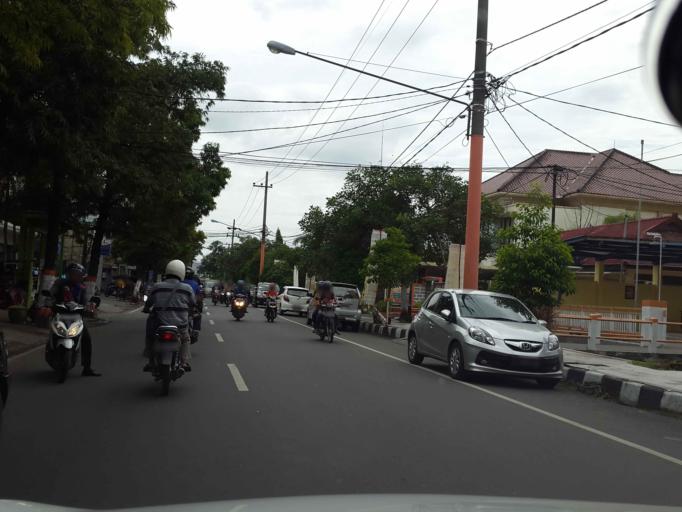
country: ID
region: East Java
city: Mojokerto
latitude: -7.4719
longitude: 112.4379
